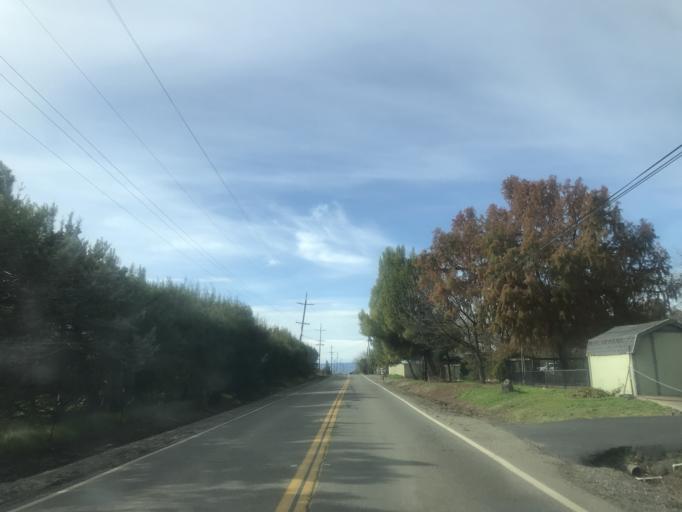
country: US
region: California
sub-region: Yolo County
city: Woodland
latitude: 38.6635
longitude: -121.8679
